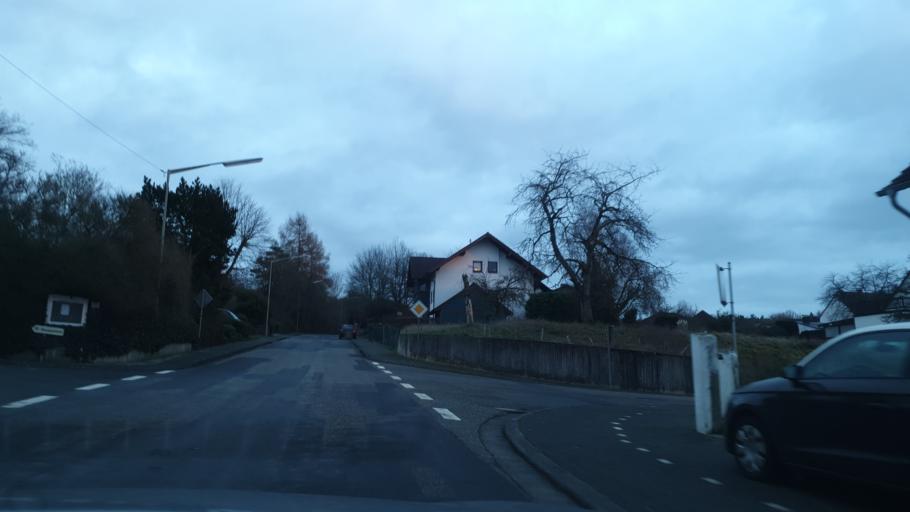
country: DE
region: Rheinland-Pfalz
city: Fluterschen
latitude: 50.6675
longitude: 7.6289
